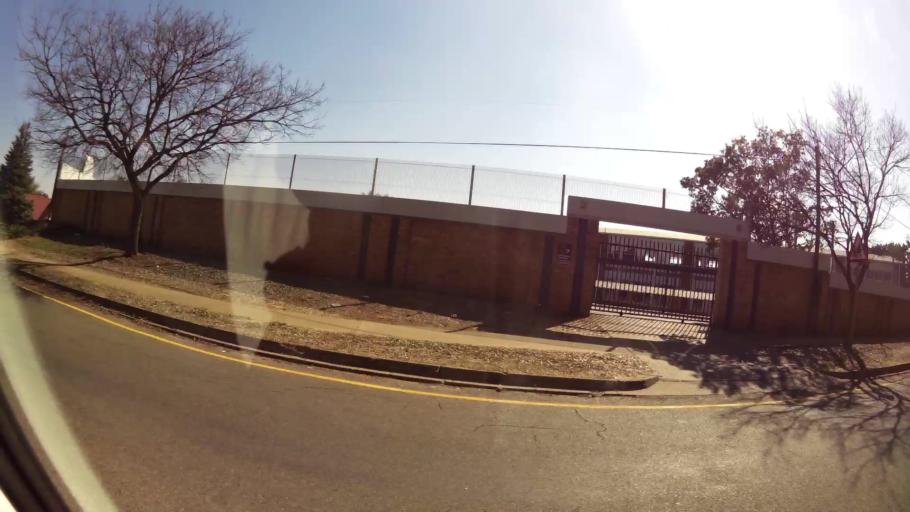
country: ZA
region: Gauteng
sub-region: City of Tshwane Metropolitan Municipality
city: Pretoria
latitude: -25.7672
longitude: 28.2588
